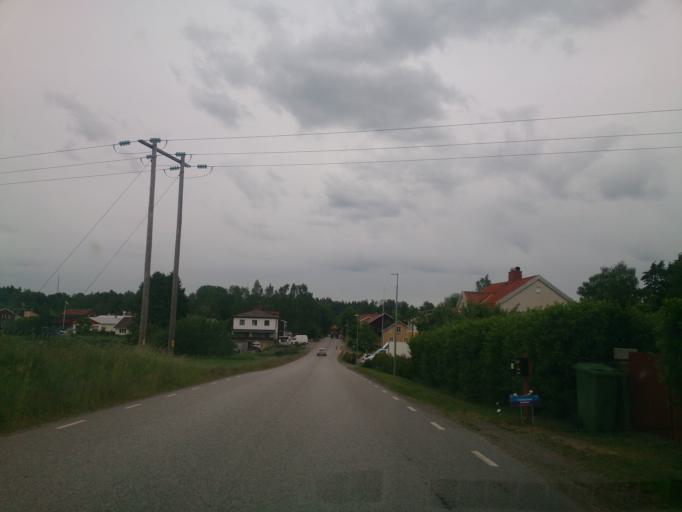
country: SE
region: OEstergoetland
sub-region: Valdemarsviks Kommun
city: Gusum
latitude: 58.3317
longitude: 16.4414
